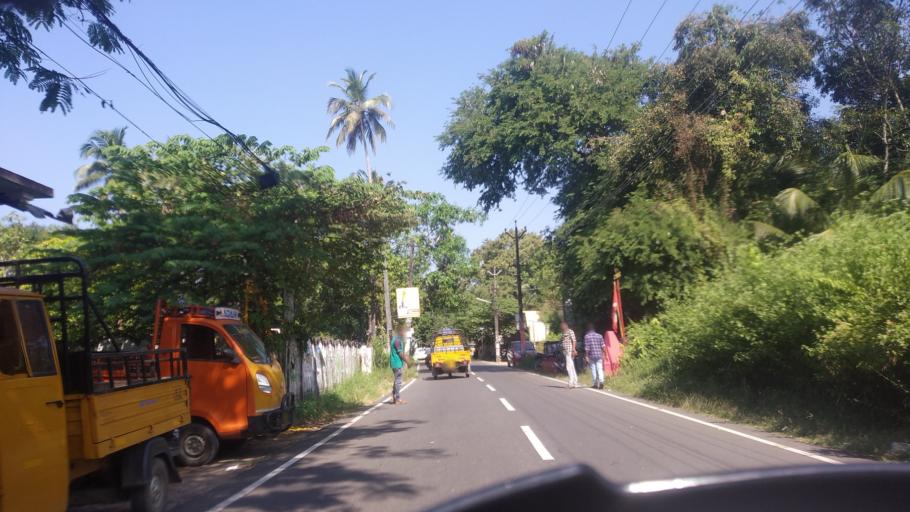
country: IN
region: Kerala
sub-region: Ernakulam
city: Elur
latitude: 10.1133
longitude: 76.2482
